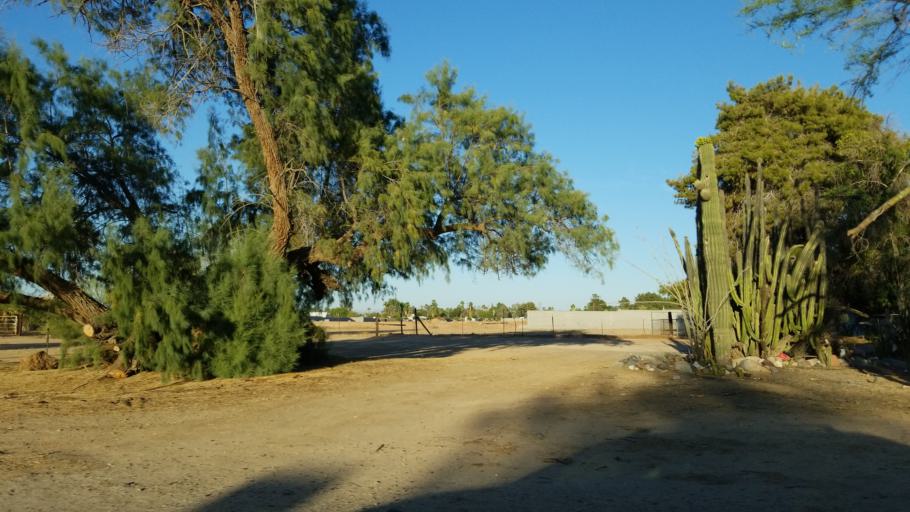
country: US
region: Arizona
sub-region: Maricopa County
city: Guadalupe
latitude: 33.3910
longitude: -112.0300
